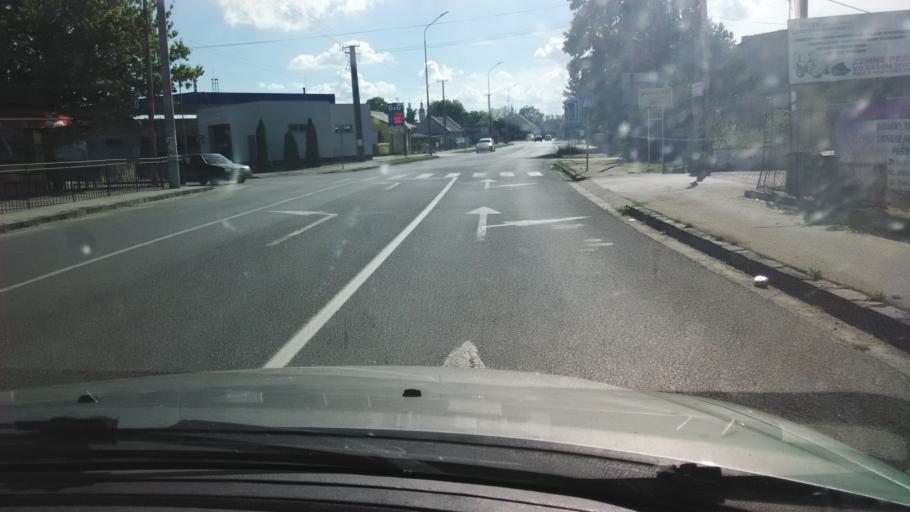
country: SK
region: Nitriansky
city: Surany
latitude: 48.0898
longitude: 18.1937
